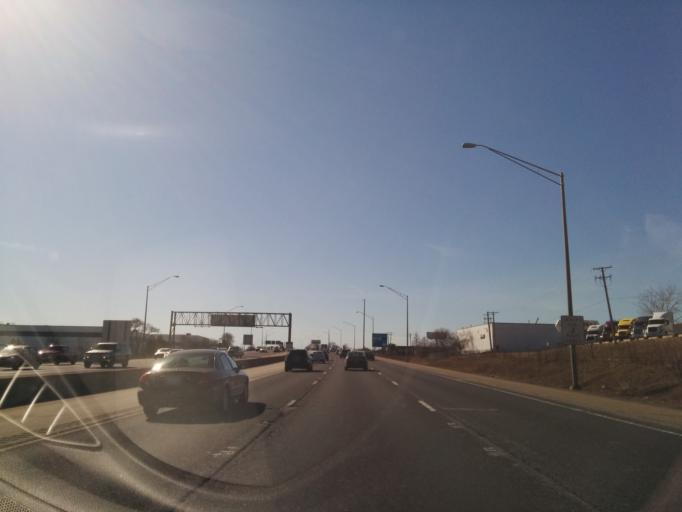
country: US
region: Illinois
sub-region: DuPage County
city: Burr Ridge
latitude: 41.7514
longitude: -87.9285
